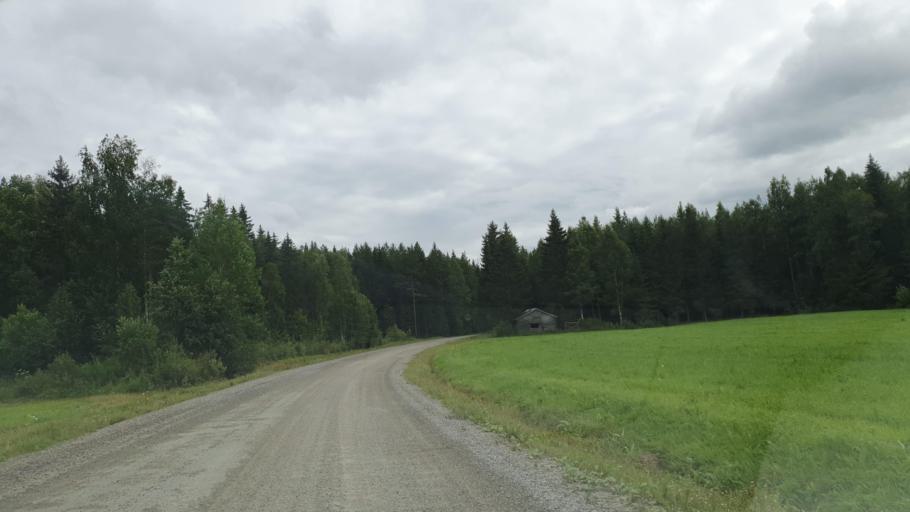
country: FI
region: Northern Savo
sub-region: Ylae-Savo
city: Iisalmi
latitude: 63.5412
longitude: 27.0712
